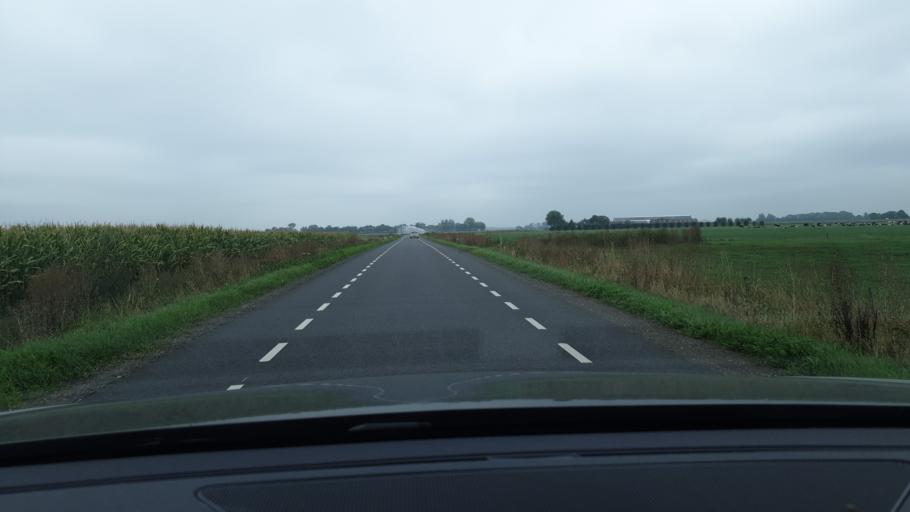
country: NL
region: Gelderland
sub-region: Gemeente Maasdriel
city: Heerewaarden
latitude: 51.7701
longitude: 5.3746
